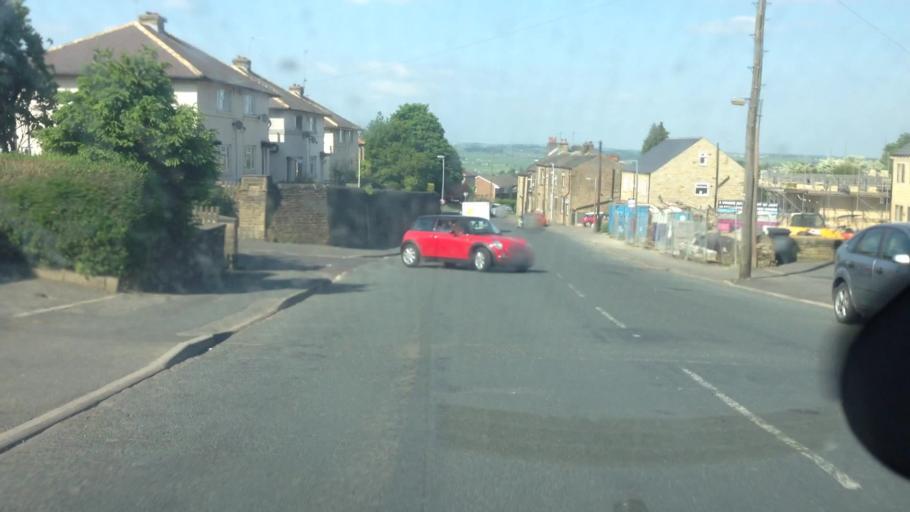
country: GB
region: England
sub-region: Calderdale
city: Brighouse
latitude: 53.6825
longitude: -1.7975
